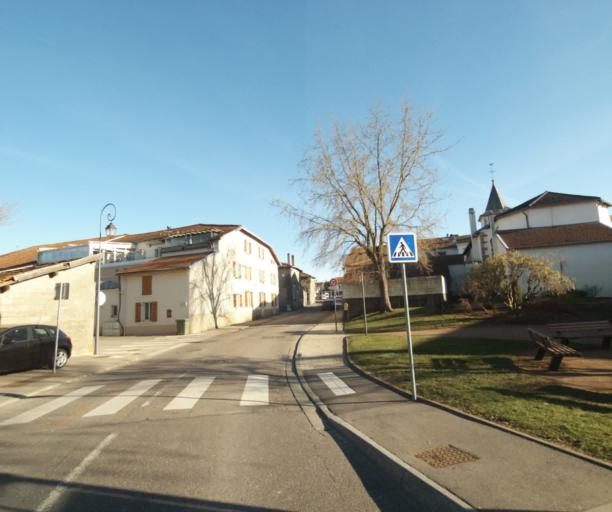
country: FR
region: Lorraine
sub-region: Departement de Meurthe-et-Moselle
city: Seichamps
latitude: 48.7169
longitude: 6.2656
